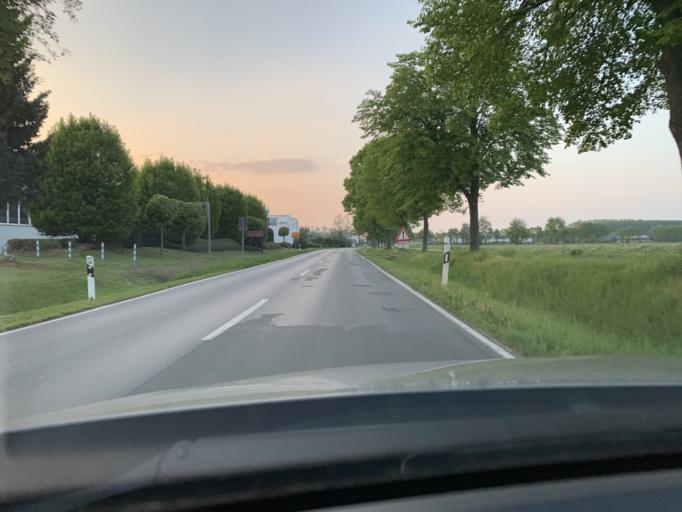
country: DE
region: North Rhine-Westphalia
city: Rietberg
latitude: 51.7623
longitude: 8.3862
